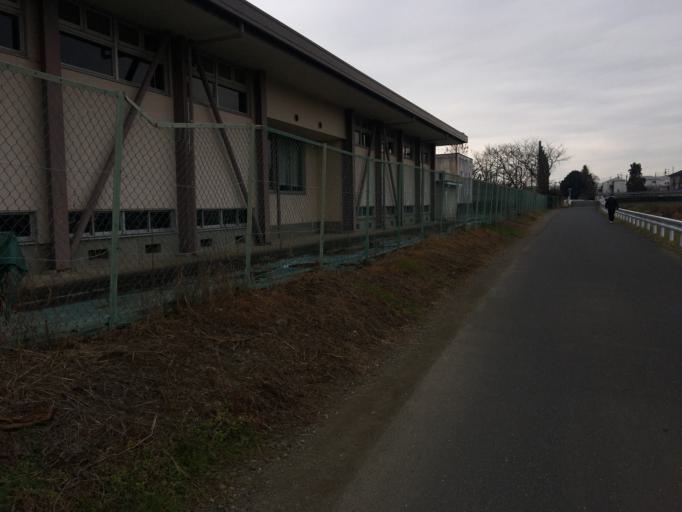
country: JP
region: Saitama
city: Sayama
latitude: 35.9056
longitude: 139.4066
